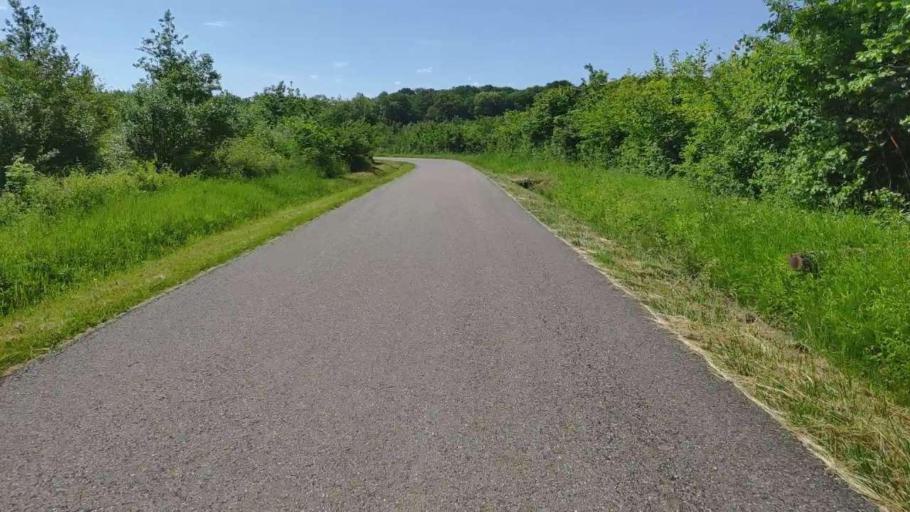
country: FR
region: Franche-Comte
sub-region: Departement du Jura
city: Bletterans
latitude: 46.7131
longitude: 5.4073
